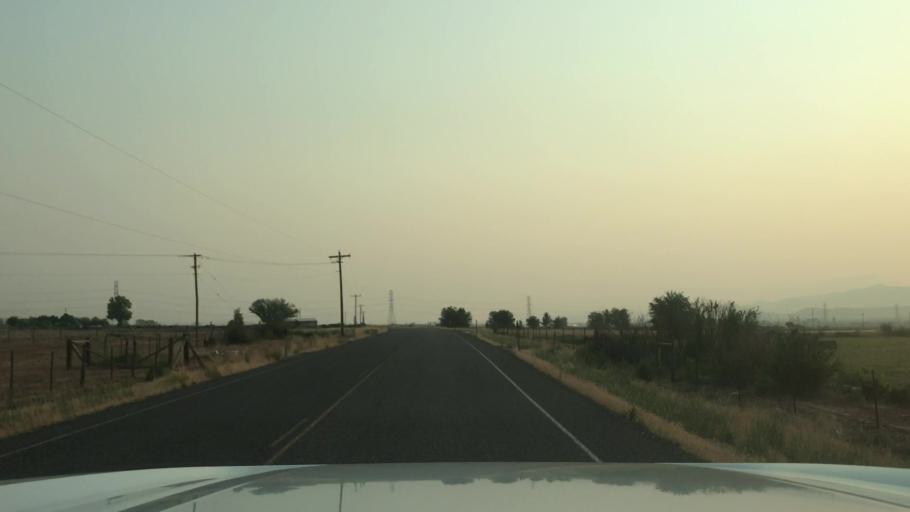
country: US
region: Utah
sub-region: Sevier County
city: Aurora
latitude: 38.8903
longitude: -111.9545
